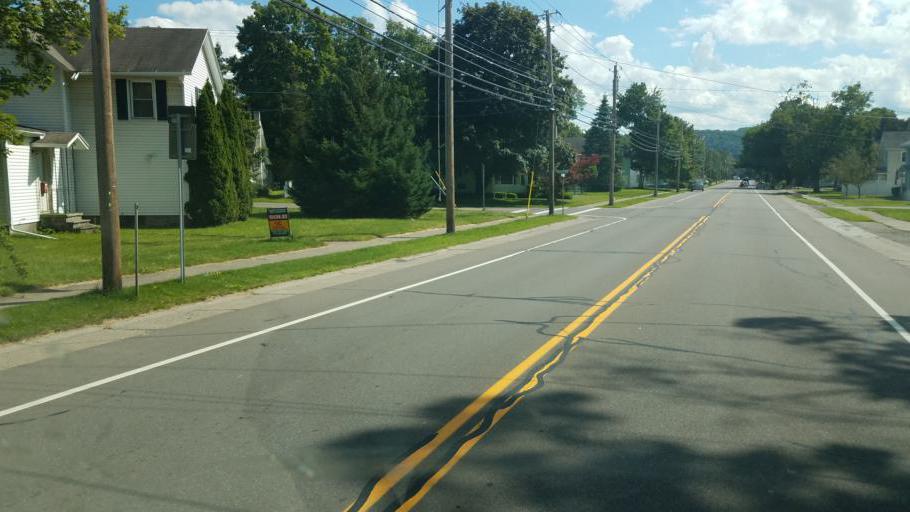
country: US
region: New York
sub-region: Steuben County
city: Bath
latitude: 42.3438
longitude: -77.3138
